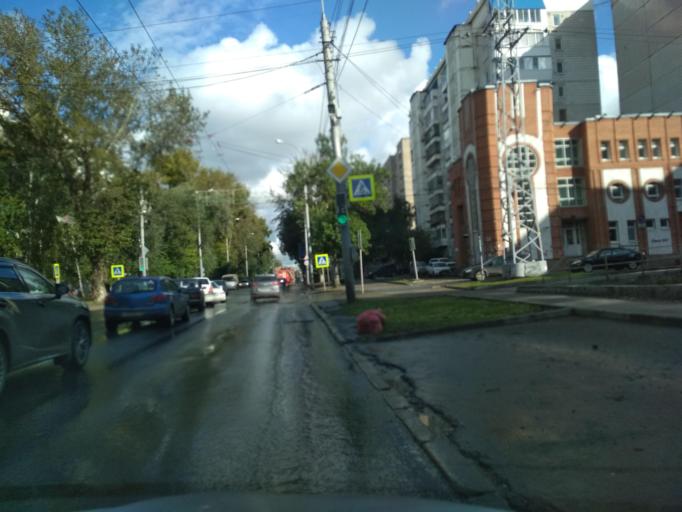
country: RU
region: Tomsk
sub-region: Tomskiy Rayon
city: Tomsk
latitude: 56.4761
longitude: 84.9753
